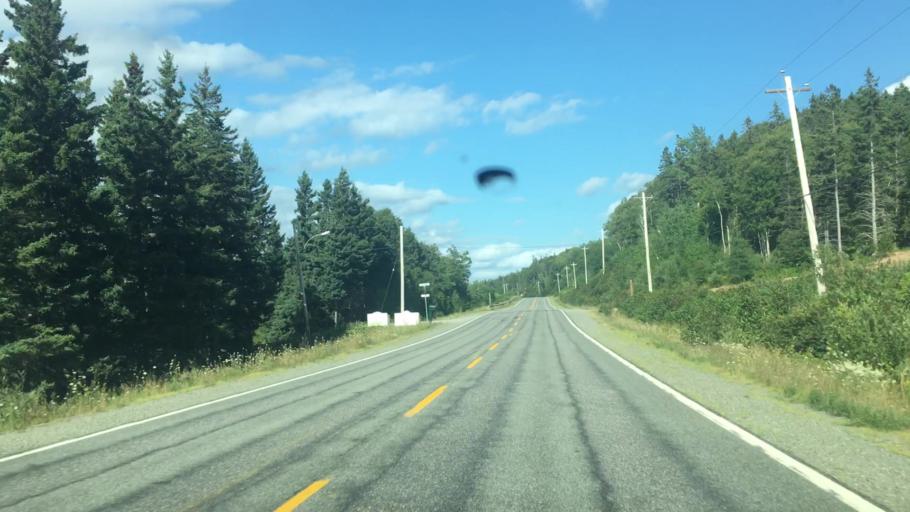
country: CA
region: Nova Scotia
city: Sydney
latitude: 45.8693
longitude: -60.6108
